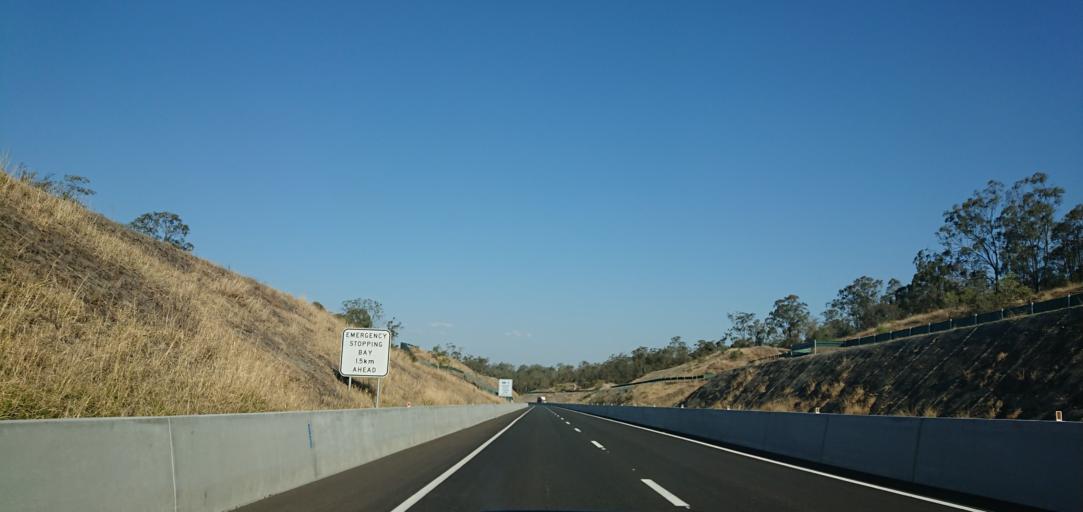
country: AU
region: Queensland
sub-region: Toowoomba
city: East Toowoomba
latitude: -27.5115
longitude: 152.0173
